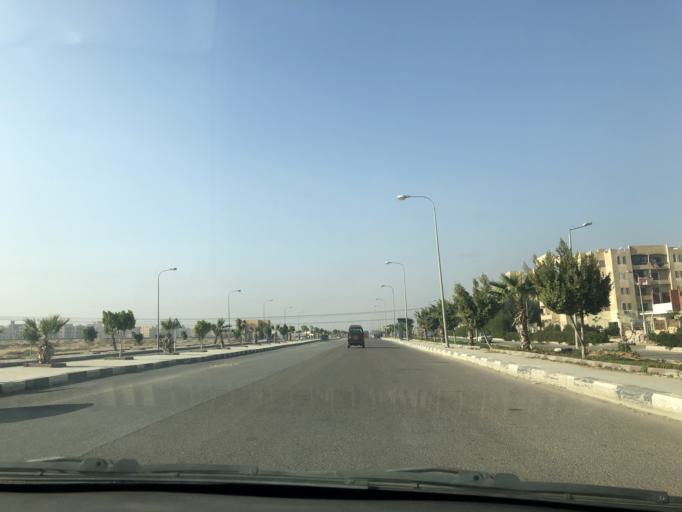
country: EG
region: Al Jizah
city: Madinat Sittah Uktubar
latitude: 29.9224
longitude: 31.0572
